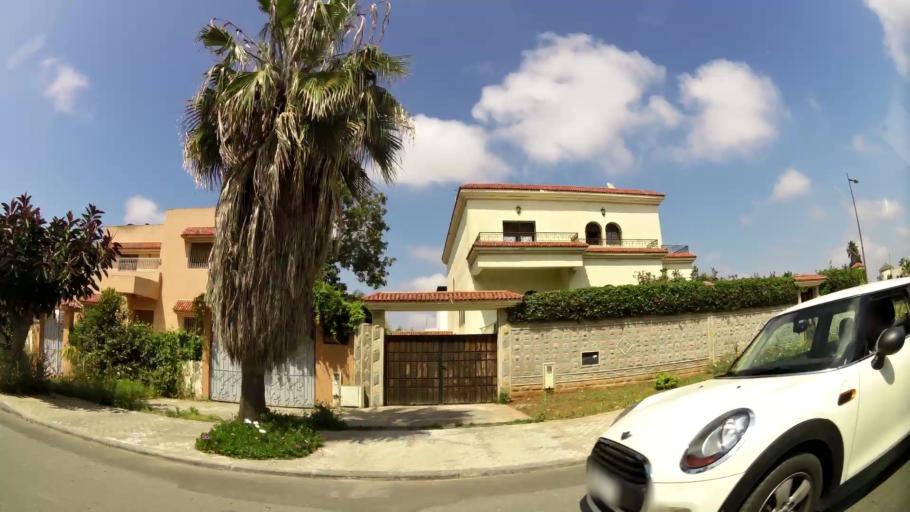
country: MA
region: Rabat-Sale-Zemmour-Zaer
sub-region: Skhirate-Temara
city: Temara
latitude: 33.9559
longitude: -6.8801
